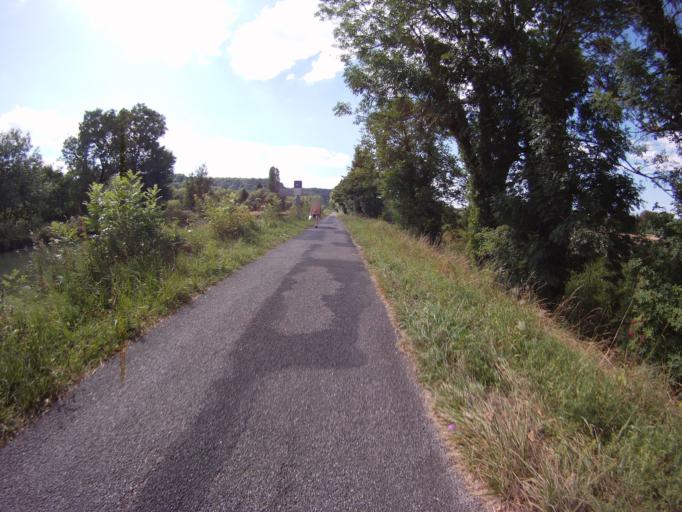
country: FR
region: Lorraine
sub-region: Departement de la Meuse
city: Longeville-en-Barrois
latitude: 48.7280
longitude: 5.2302
